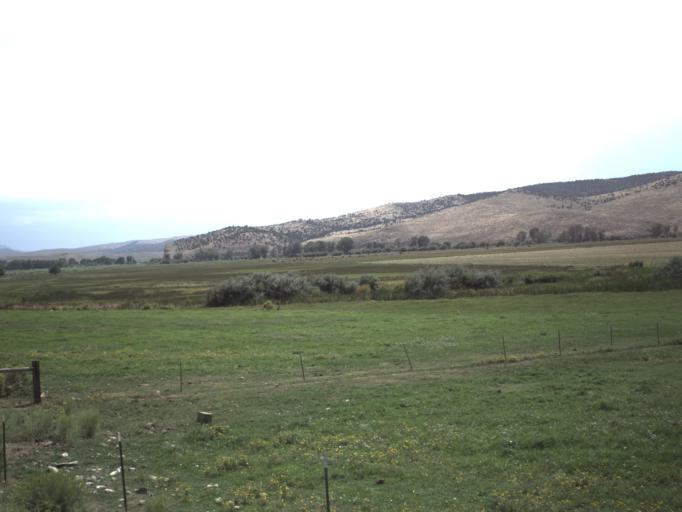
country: US
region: Utah
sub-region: Piute County
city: Junction
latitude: 38.1128
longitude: -111.9911
